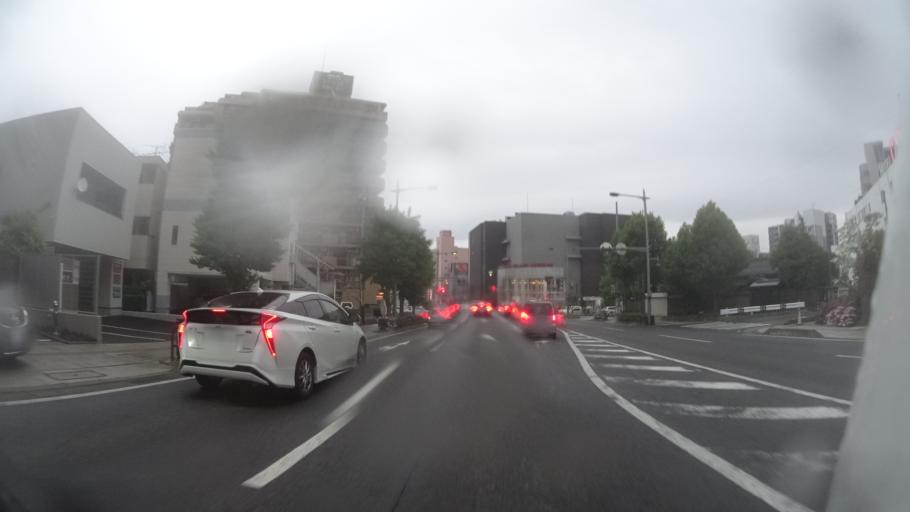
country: JP
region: Nagano
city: Nagano-shi
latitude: 36.6551
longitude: 138.1915
